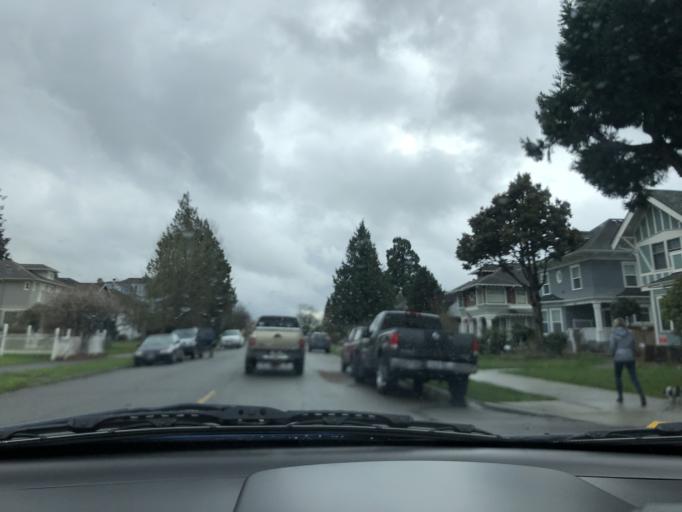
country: US
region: Washington
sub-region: Snohomish County
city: Everett
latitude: 47.9901
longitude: -122.2111
